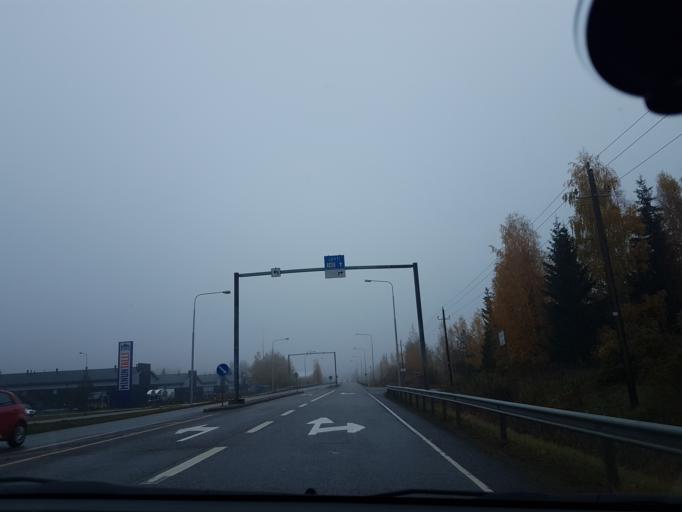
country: FI
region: Uusimaa
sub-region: Helsinki
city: Jaervenpaeae
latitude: 60.4624
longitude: 25.1393
